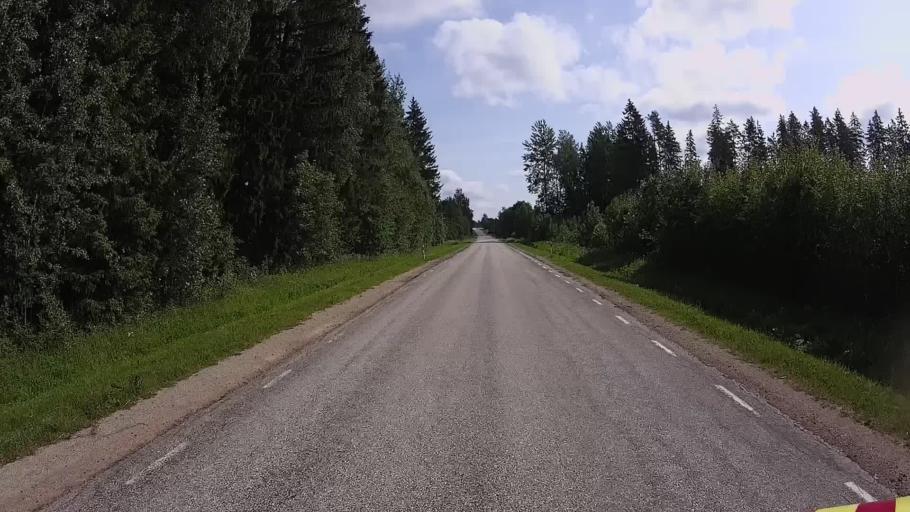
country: EE
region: Vorumaa
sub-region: Antsla vald
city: Vana-Antsla
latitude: 57.8480
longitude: 26.5724
